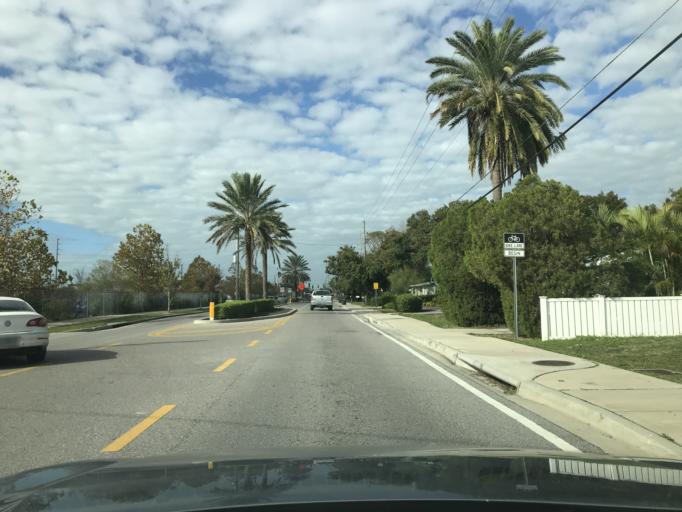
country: US
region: Florida
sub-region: Pinellas County
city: Largo
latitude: 27.9278
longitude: -82.7851
